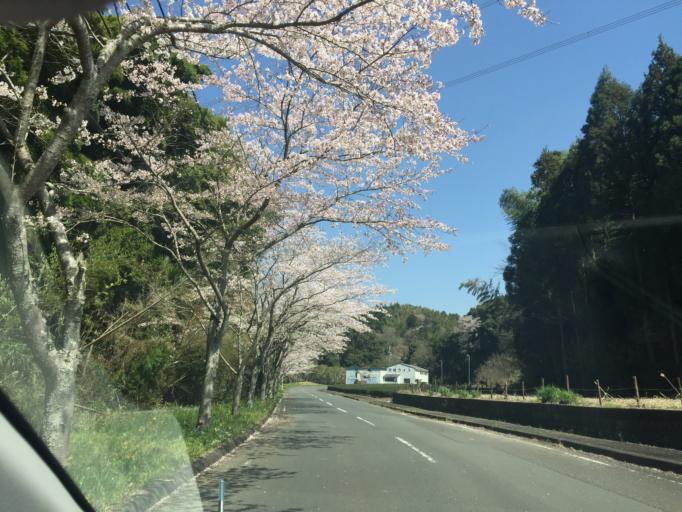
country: JP
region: Shizuoka
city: Kanaya
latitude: 34.7835
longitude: 138.1175
